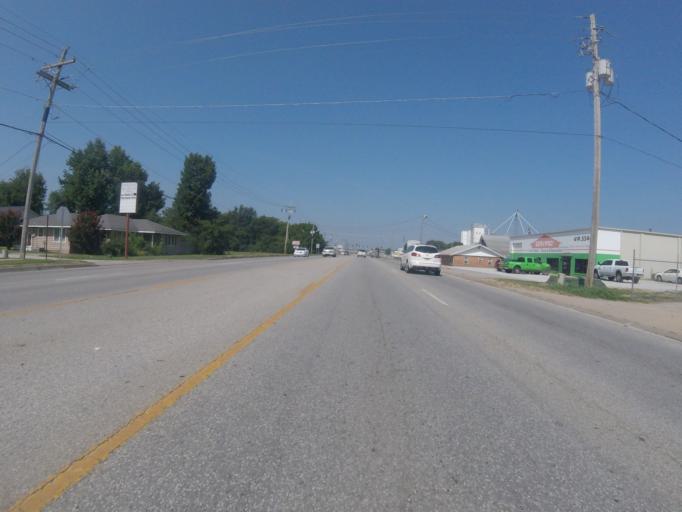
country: US
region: Arkansas
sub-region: Washington County
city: Springdale
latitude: 36.1672
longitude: -94.1320
